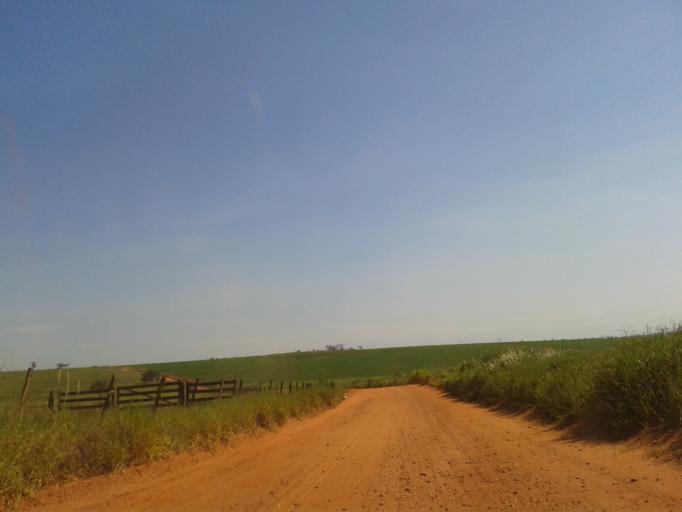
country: BR
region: Minas Gerais
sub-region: Santa Vitoria
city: Santa Vitoria
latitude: -19.0764
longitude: -50.4813
